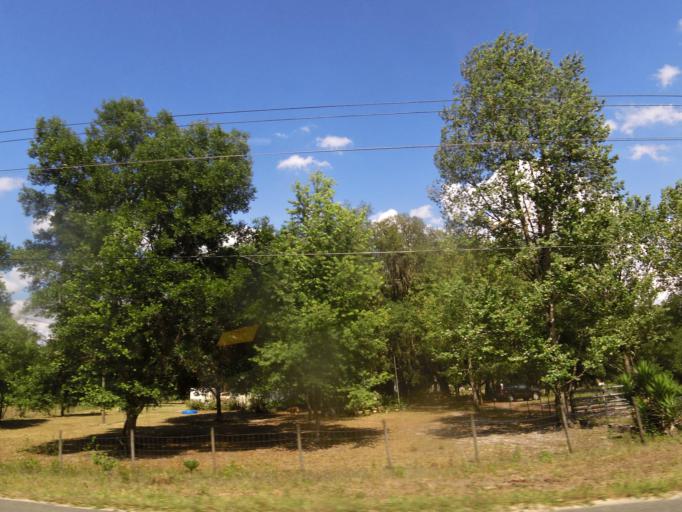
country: US
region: Florida
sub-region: Clay County
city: Keystone Heights
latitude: 29.8303
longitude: -81.9225
